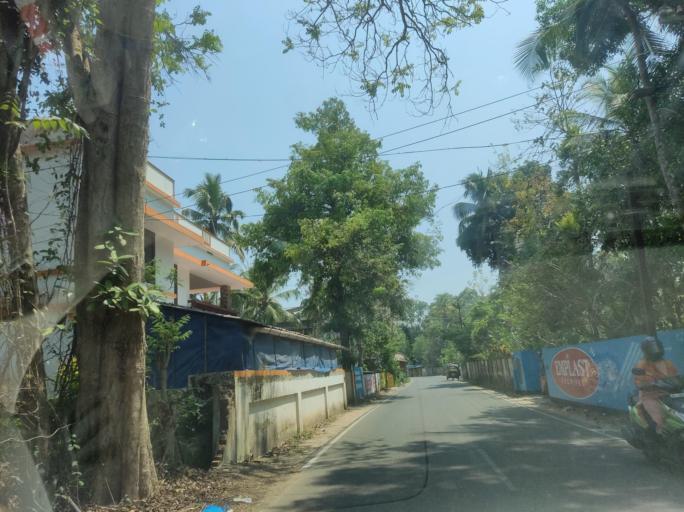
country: IN
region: Kerala
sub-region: Alappuzha
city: Kutiatodu
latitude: 9.8298
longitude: 76.2977
